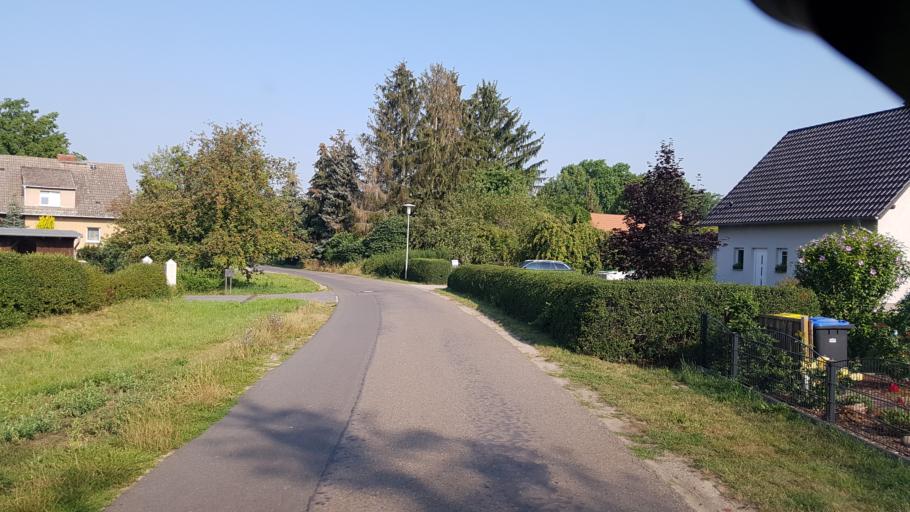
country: DE
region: Brandenburg
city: Drebkau
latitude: 51.6916
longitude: 14.2516
